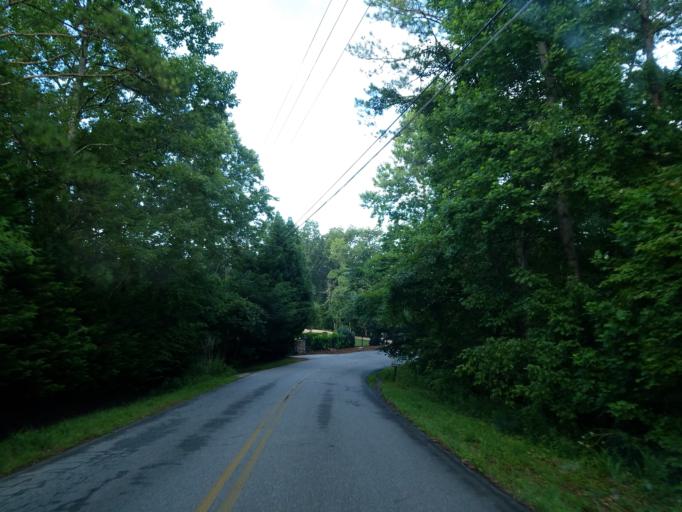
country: US
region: Georgia
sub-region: Bartow County
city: Emerson
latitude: 34.0945
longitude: -84.7480
